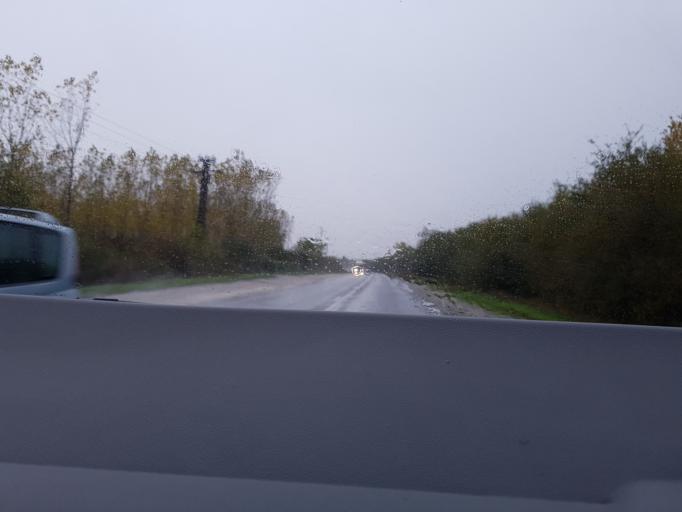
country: FR
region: Aquitaine
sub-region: Departement de la Gironde
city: Saint-Louis-de-Montferrand
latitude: 44.9511
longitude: -0.5188
